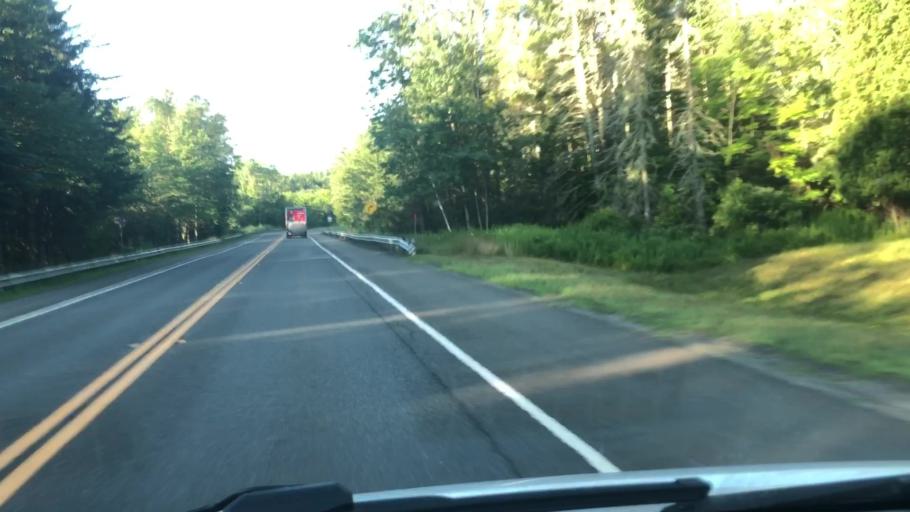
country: US
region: Massachusetts
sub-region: Hampshire County
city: Chesterfield
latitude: 42.4440
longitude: -72.8602
